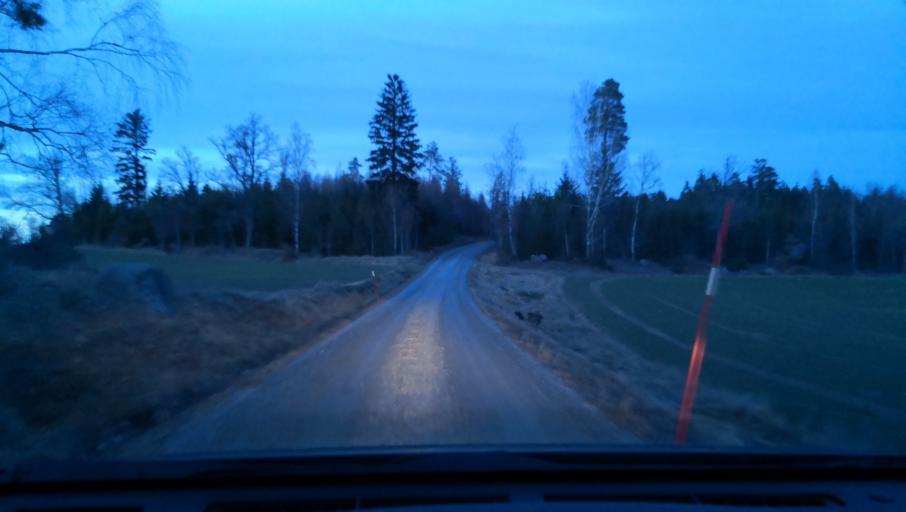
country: SE
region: Uppsala
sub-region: Enkopings Kommun
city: Dalby
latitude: 59.5614
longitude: 17.3714
